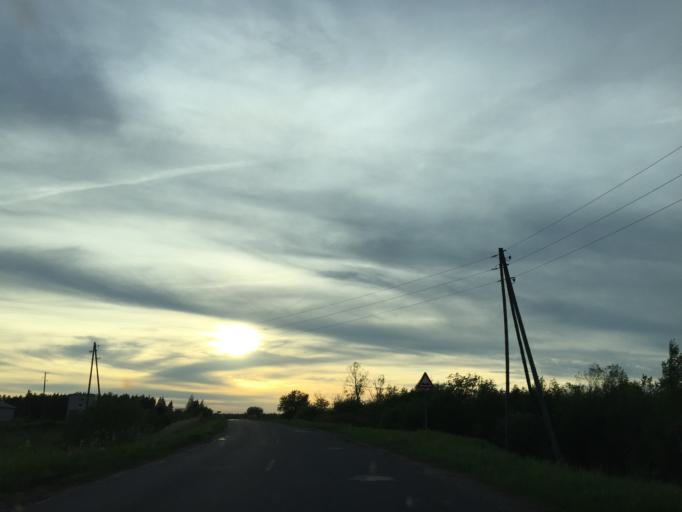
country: LV
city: Tireli
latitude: 56.8096
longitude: 23.5824
